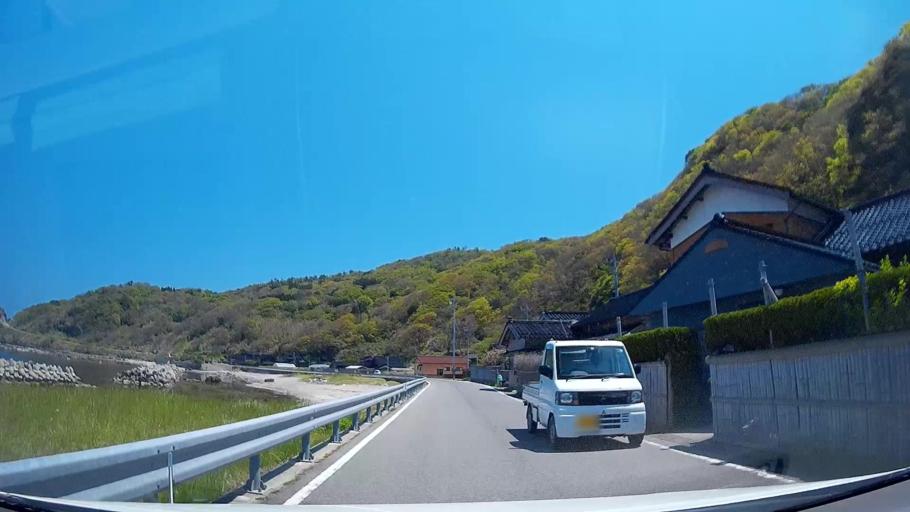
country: JP
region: Ishikawa
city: Nanao
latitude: 37.5192
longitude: 137.2435
